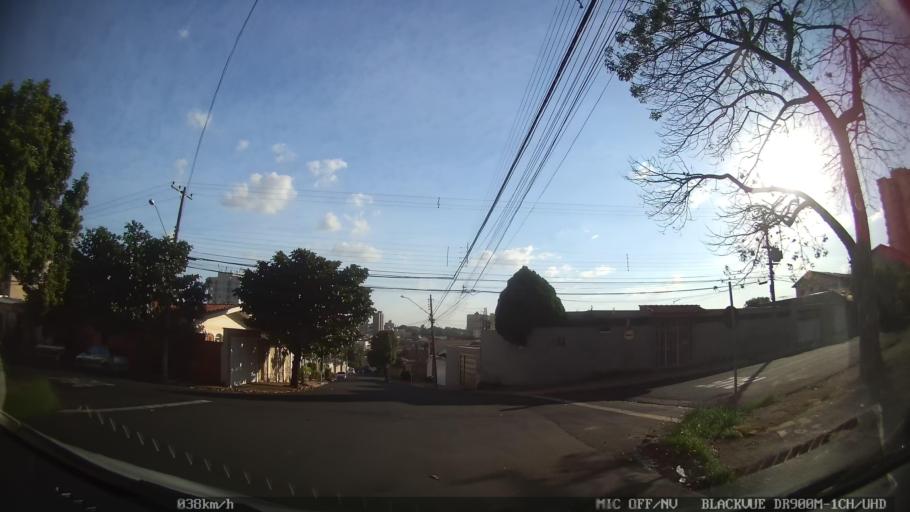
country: BR
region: Sao Paulo
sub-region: Ribeirao Preto
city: Ribeirao Preto
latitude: -21.1869
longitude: -47.7936
